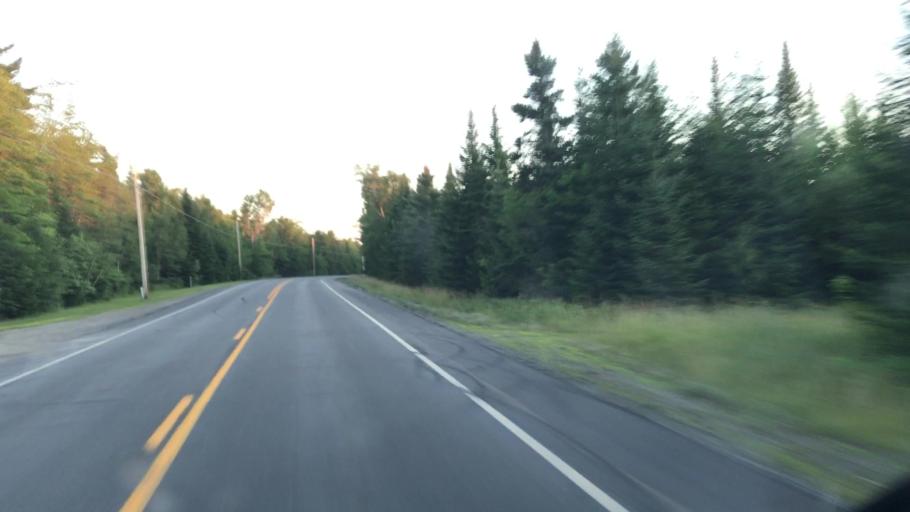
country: US
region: Maine
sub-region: Penobscot County
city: Medway
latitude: 45.5689
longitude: -68.3218
